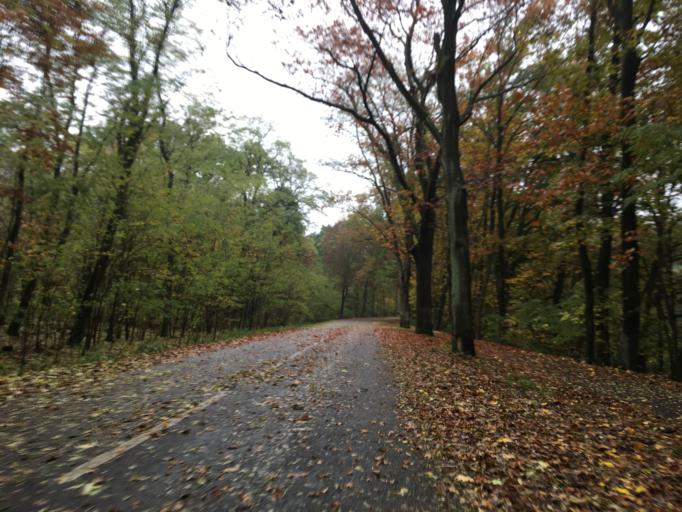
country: DE
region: Brandenburg
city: Beeskow
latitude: 52.1577
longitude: 14.2224
